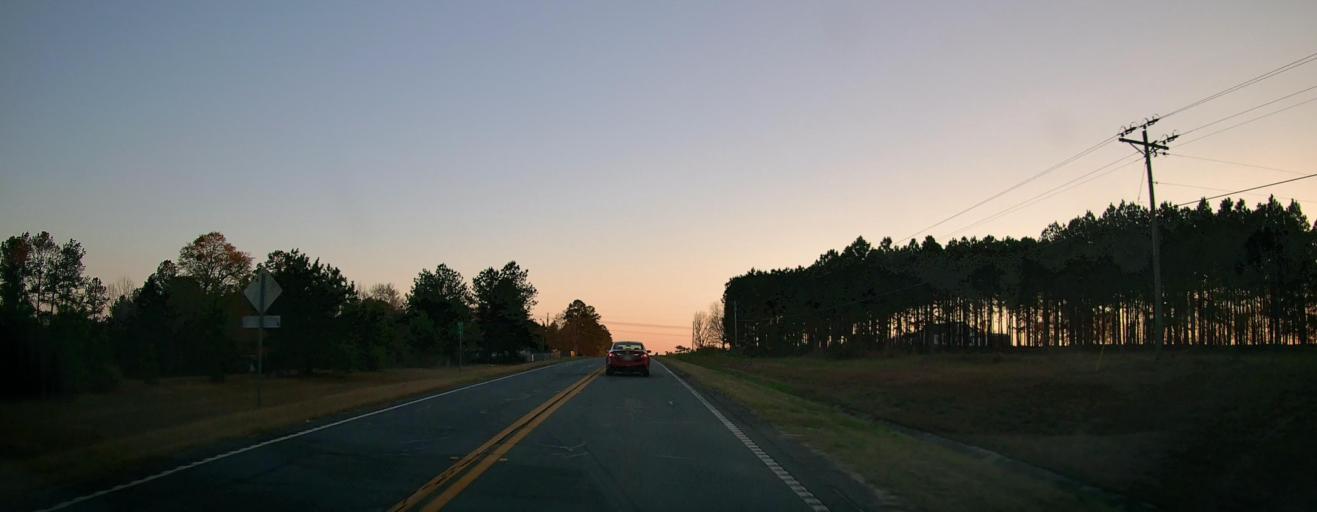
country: US
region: Georgia
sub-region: Dodge County
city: Eastman
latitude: 32.2520
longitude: -83.1415
